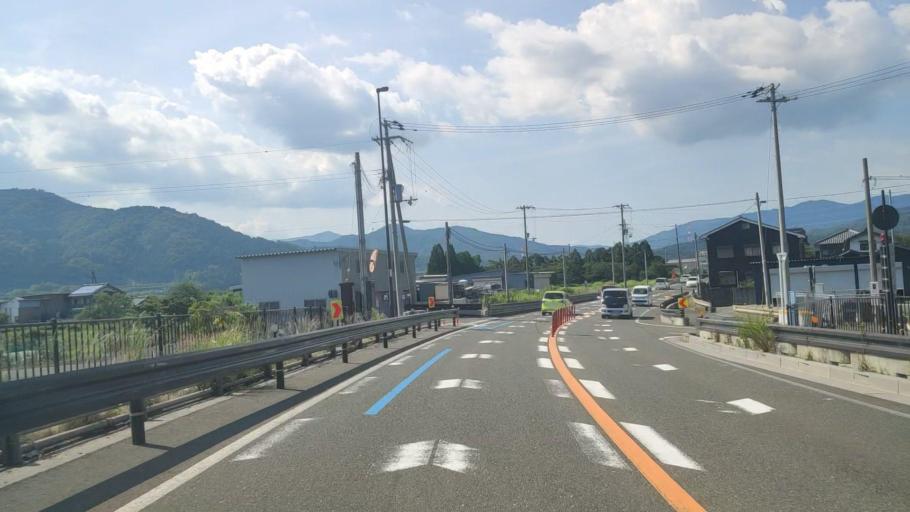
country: JP
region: Shiga Prefecture
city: Nagahama
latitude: 35.5149
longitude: 136.1652
